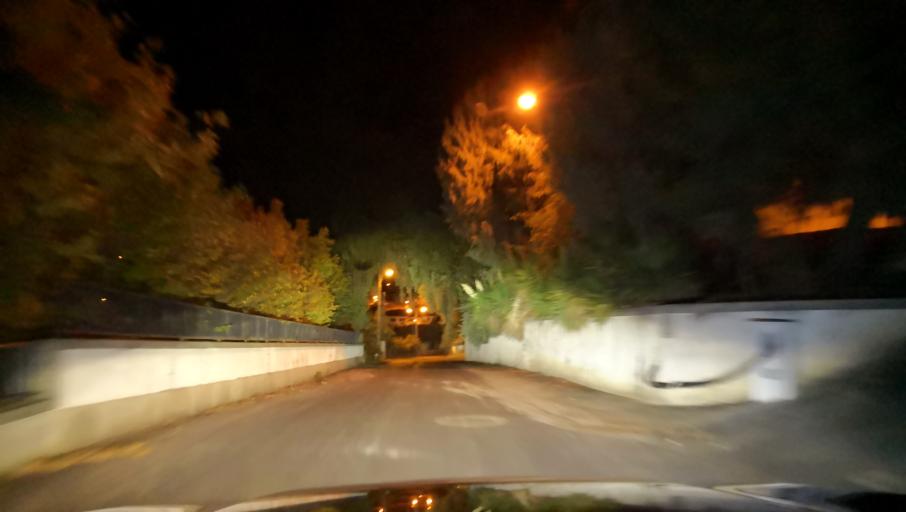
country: PT
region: Vila Real
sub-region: Sabrosa
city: Vilela
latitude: 41.2064
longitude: -7.6936
